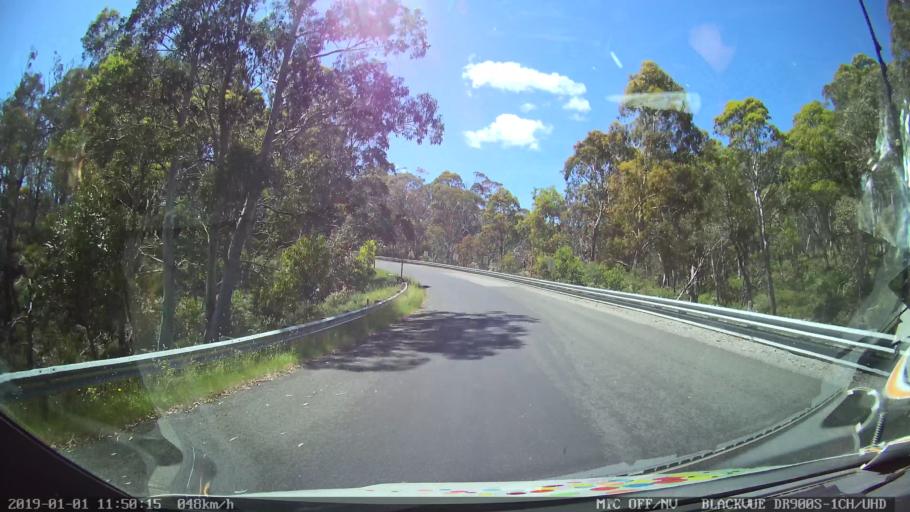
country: AU
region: New South Wales
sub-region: Snowy River
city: Jindabyne
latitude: -35.8908
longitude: 148.4193
